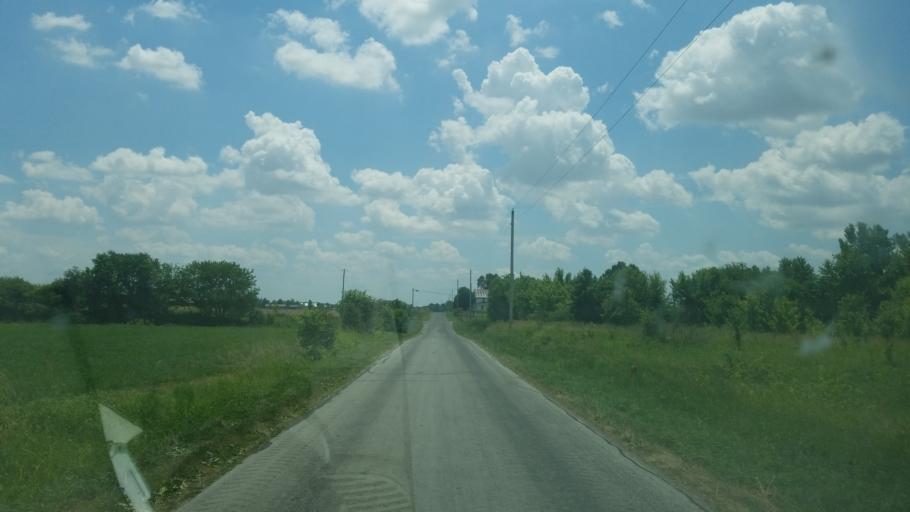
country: US
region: Ohio
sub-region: Hardin County
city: Kenton
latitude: 40.6148
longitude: -83.5590
